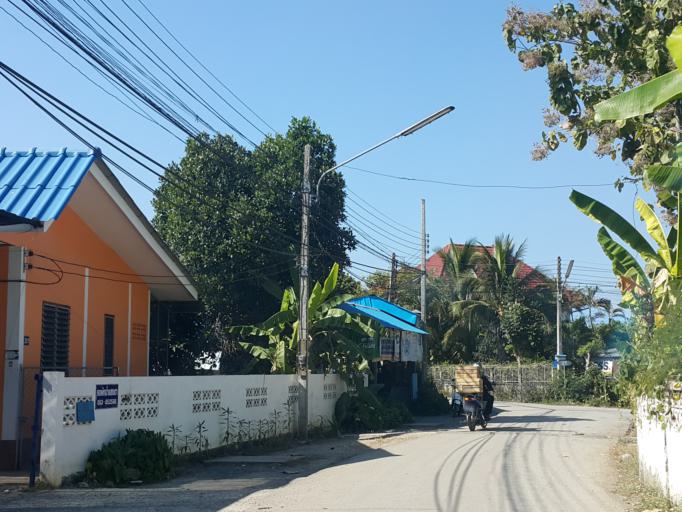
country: TH
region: Chiang Mai
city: San Sai
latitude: 18.8536
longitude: 98.9928
